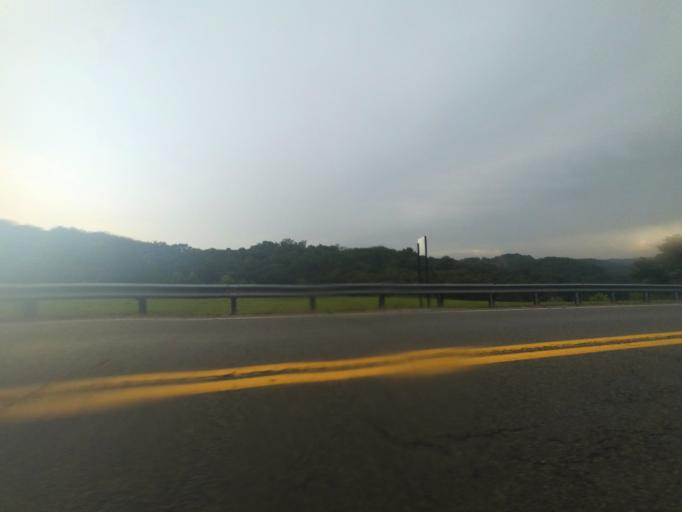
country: US
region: West Virginia
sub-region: Cabell County
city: Huntington
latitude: 38.3896
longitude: -82.3946
